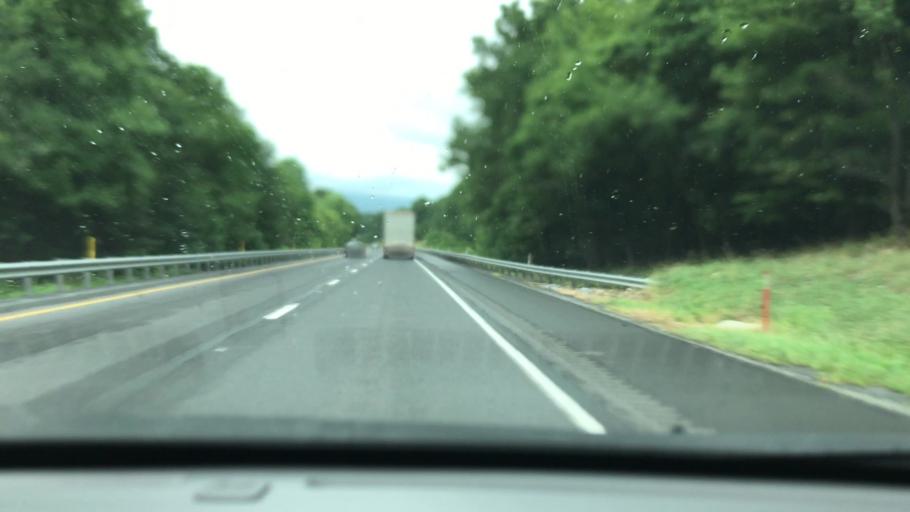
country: US
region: Pennsylvania
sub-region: Bedford County
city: Earlston
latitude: 39.8971
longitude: -78.2405
